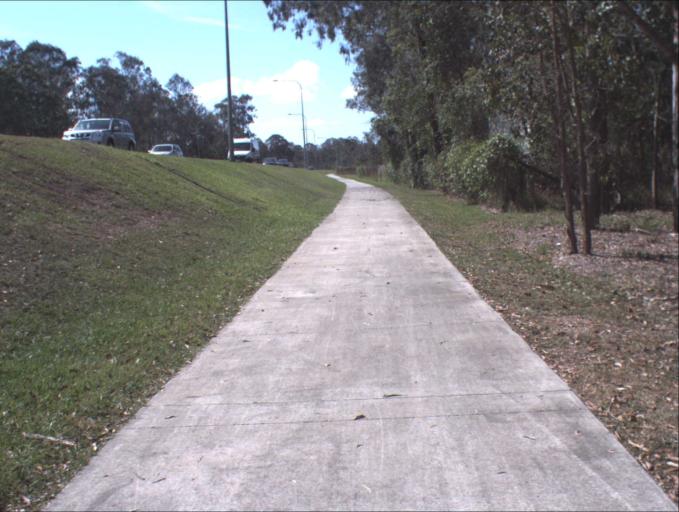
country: AU
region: Queensland
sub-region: Logan
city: Slacks Creek
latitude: -27.6526
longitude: 153.1457
